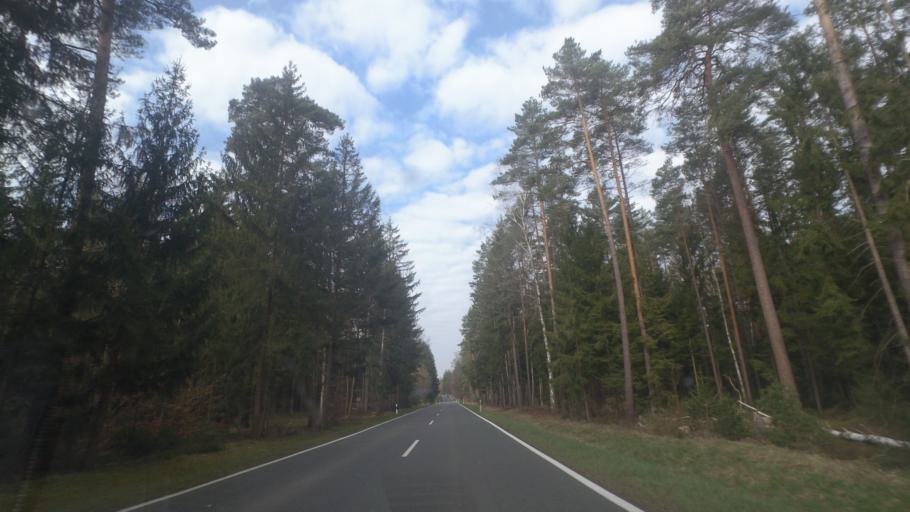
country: DE
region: Bavaria
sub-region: Regierungsbezirk Mittelfranken
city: Feucht
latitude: 49.4187
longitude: 11.2313
